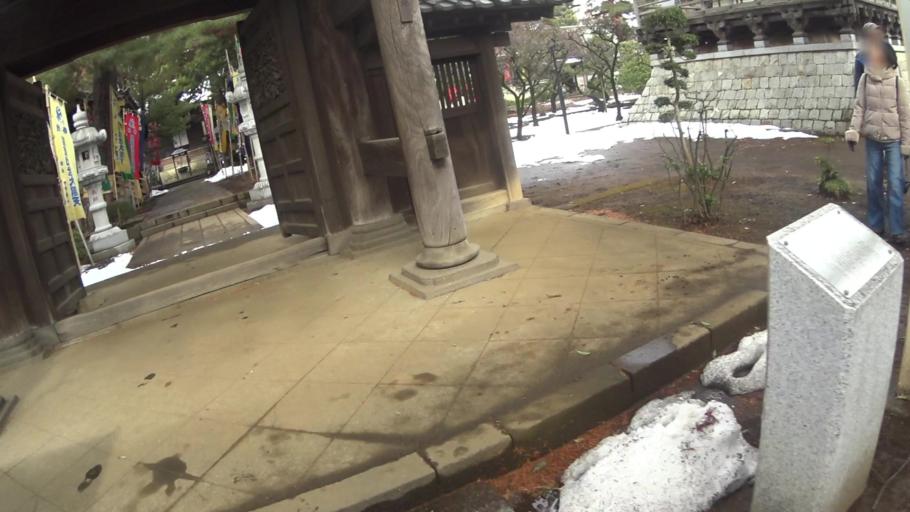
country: JP
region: Tokyo
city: Musashino
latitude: 35.7354
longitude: 139.5980
